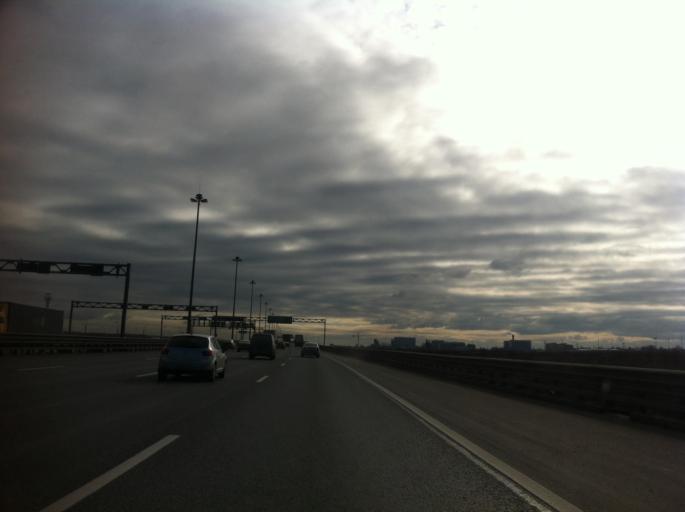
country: RU
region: St.-Petersburg
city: Dachnoye
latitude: 59.8253
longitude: 30.2931
